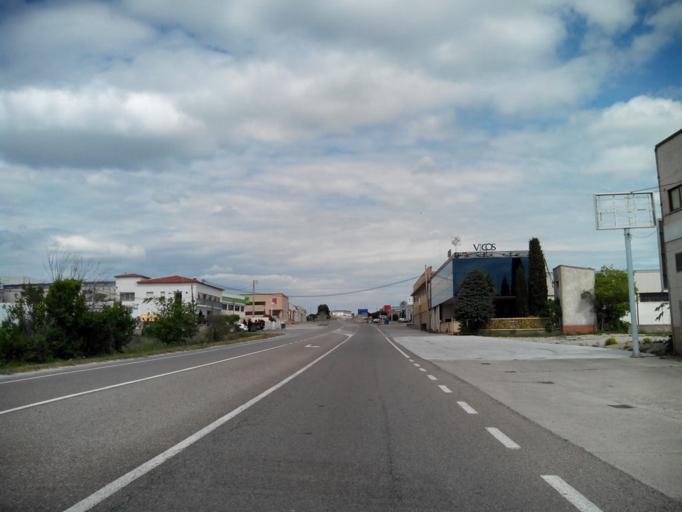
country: ES
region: Catalonia
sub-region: Provincia de Lleida
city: Tarrega
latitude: 41.6540
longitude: 1.1537
